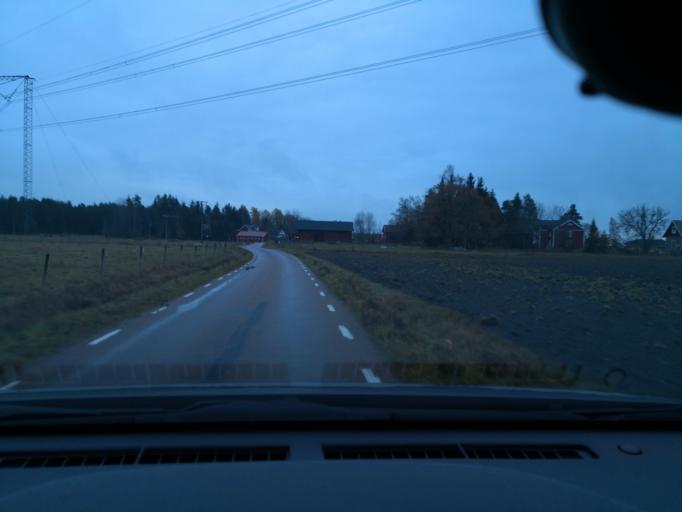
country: SE
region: Vaestmanland
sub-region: Hallstahammars Kommun
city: Kolback
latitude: 59.5682
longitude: 16.1910
